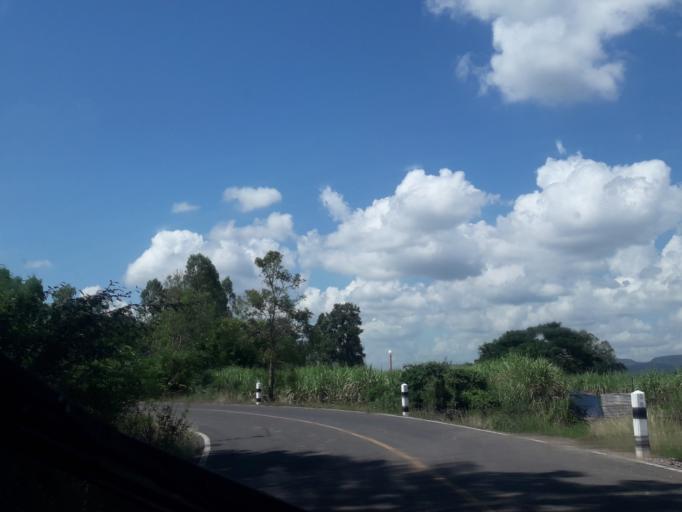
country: TH
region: Lop Buri
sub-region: Amphoe Tha Luang
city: Tha Luang
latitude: 15.0709
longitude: 101.0392
